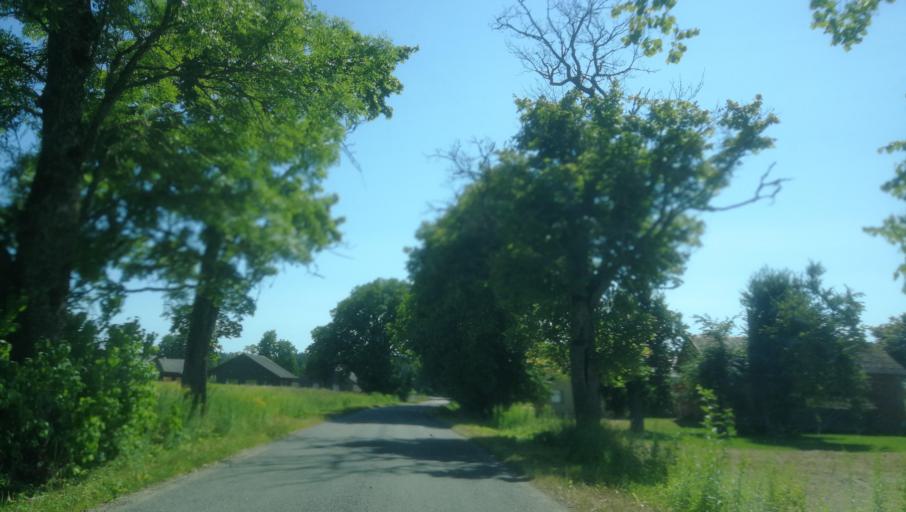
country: LV
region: Cesu Rajons
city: Cesis
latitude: 57.2947
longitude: 25.2337
